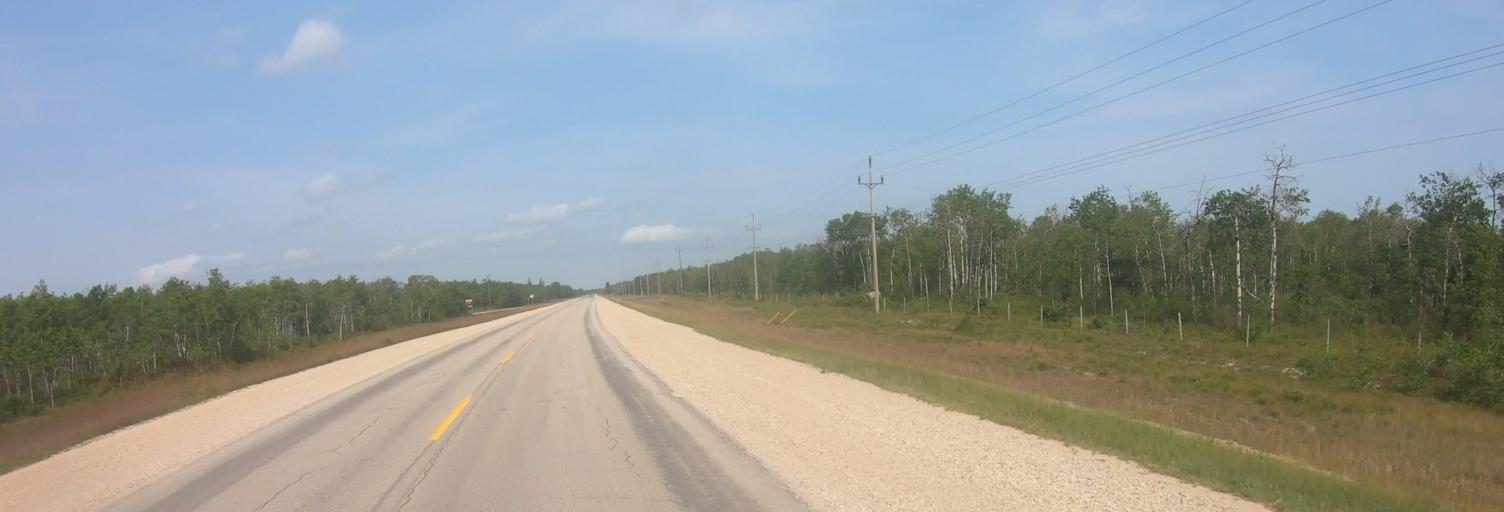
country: CA
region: Manitoba
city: Steinbach
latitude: 49.3575
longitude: -96.6656
